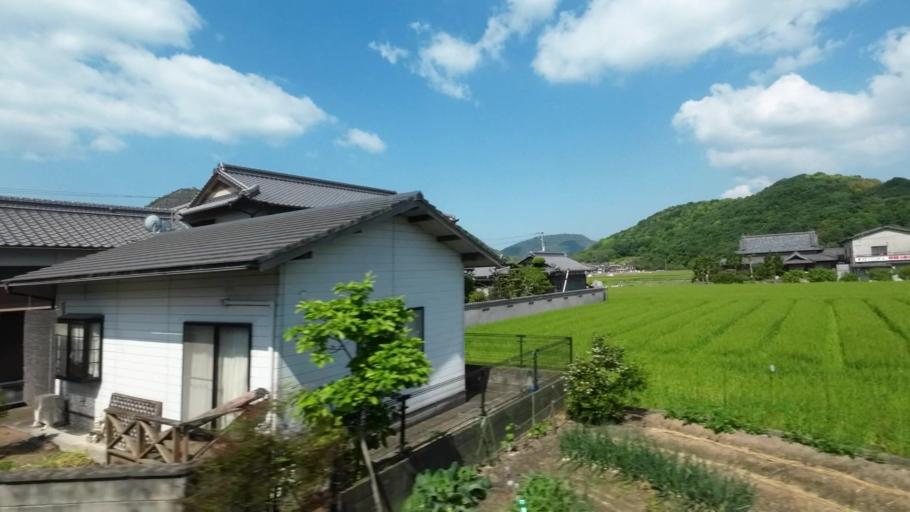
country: JP
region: Kagawa
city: Tadotsu
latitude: 34.1914
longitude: 133.7131
